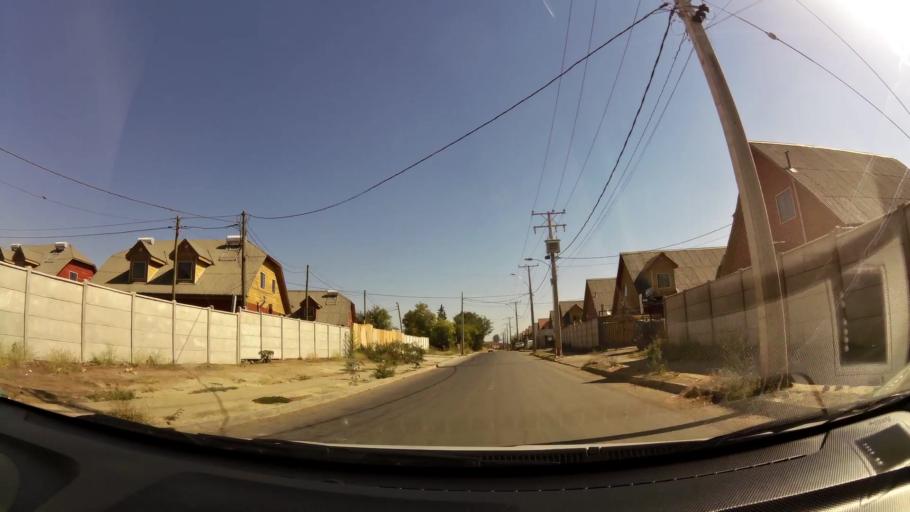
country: CL
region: Maule
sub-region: Provincia de Talca
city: Talca
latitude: -35.4078
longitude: -71.6176
